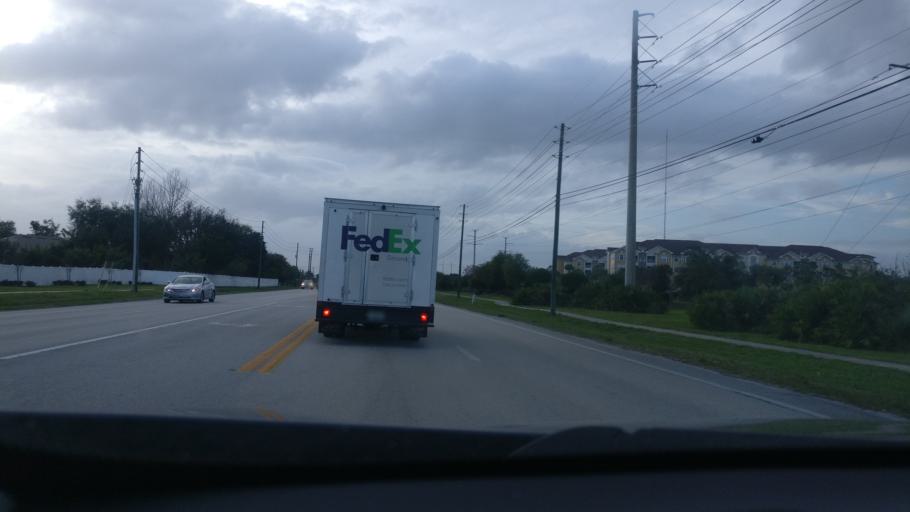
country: US
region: Florida
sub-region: Volusia County
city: DeBary
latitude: 28.9119
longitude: -81.2982
